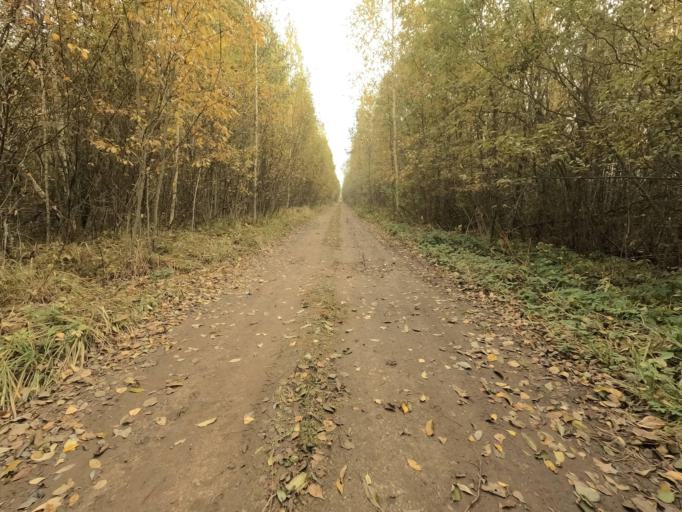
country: RU
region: Novgorod
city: Pankovka
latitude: 58.8783
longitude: 30.8587
